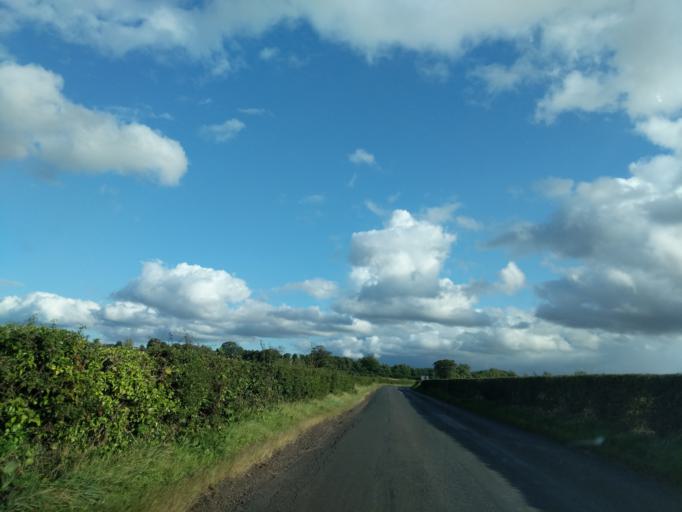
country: GB
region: Scotland
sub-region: East Lothian
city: Longniddry
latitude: 55.9719
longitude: -2.8948
